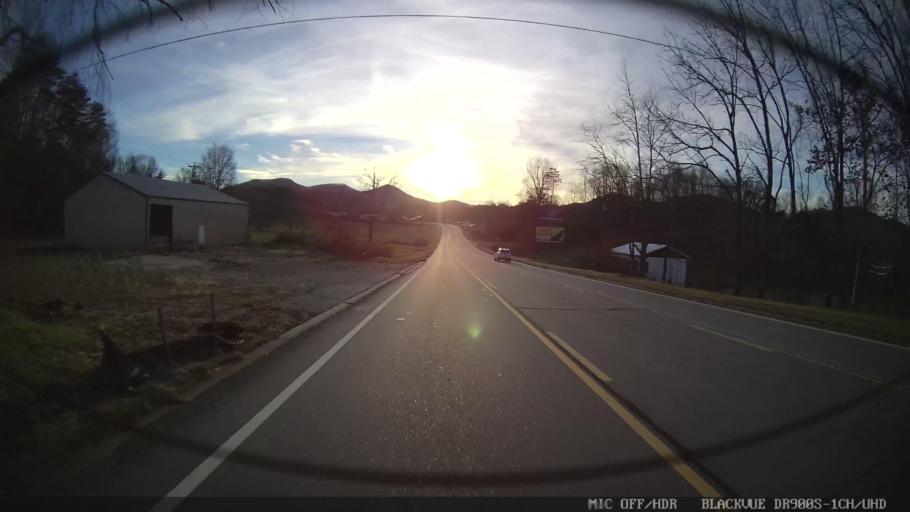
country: US
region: Georgia
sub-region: Towns County
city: Hiawassee
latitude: 34.9174
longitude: -83.8588
